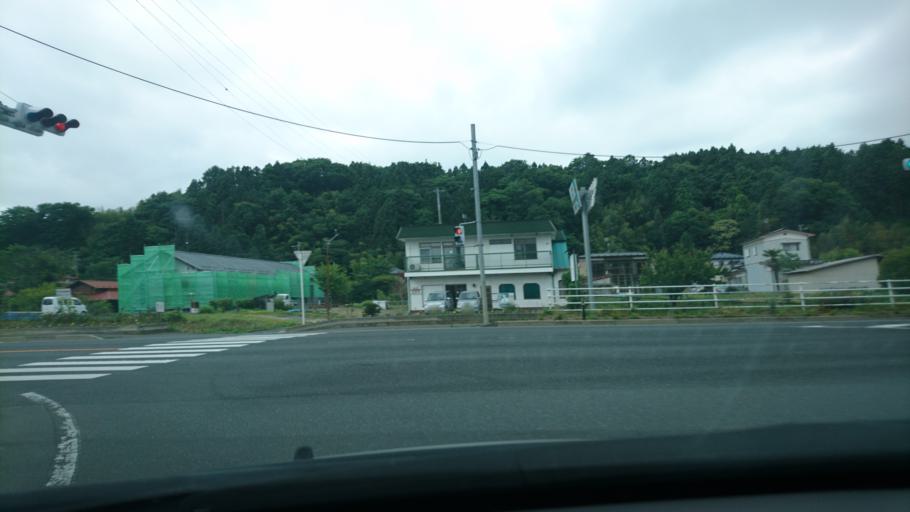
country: JP
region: Miyagi
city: Furukawa
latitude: 38.7515
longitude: 141.0178
